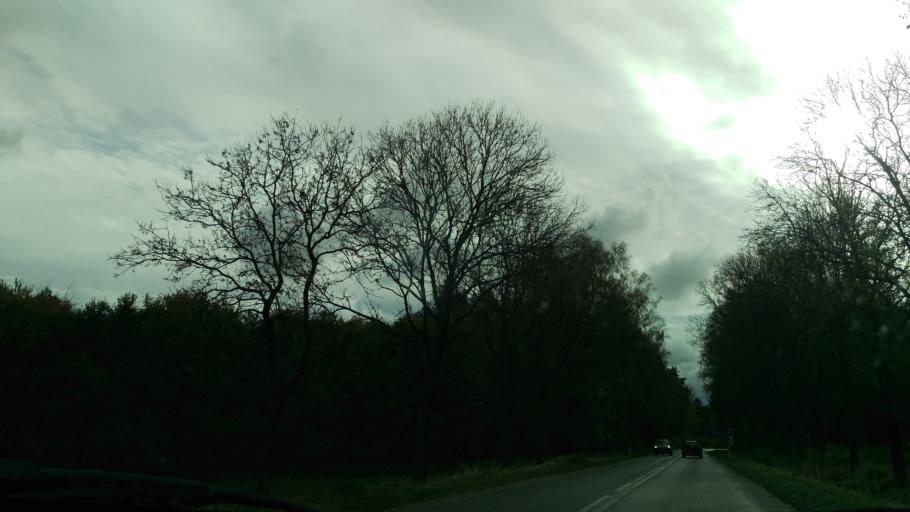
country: PL
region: West Pomeranian Voivodeship
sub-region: Powiat gryficki
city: Gryfice
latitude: 53.8606
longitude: 15.2241
